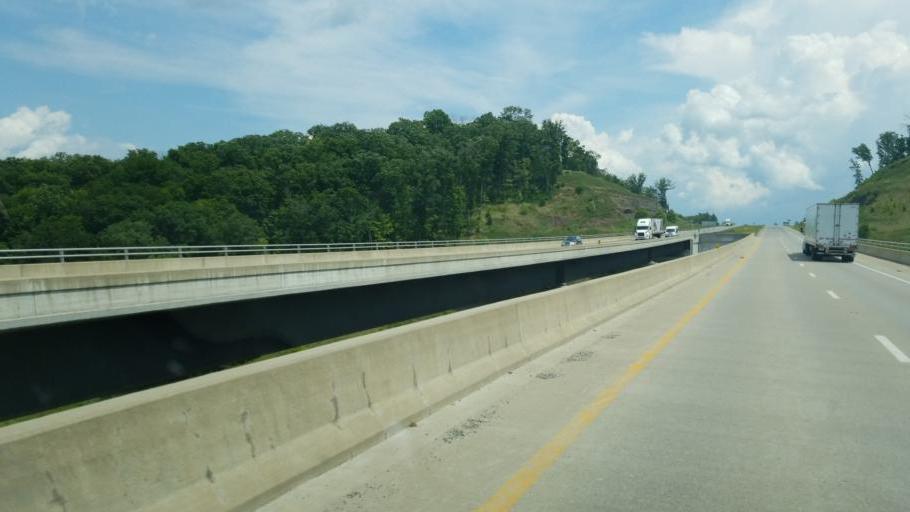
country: US
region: West Virginia
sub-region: Putnam County
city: Buffalo
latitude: 38.5559
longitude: -82.0020
